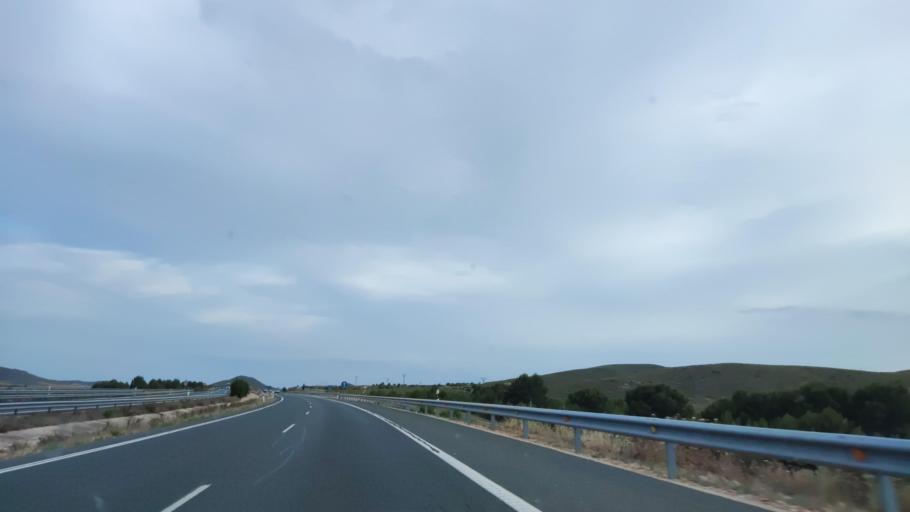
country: ES
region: Castille-La Mancha
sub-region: Provincia de Albacete
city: Tobarra
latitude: 38.5748
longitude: -1.6881
